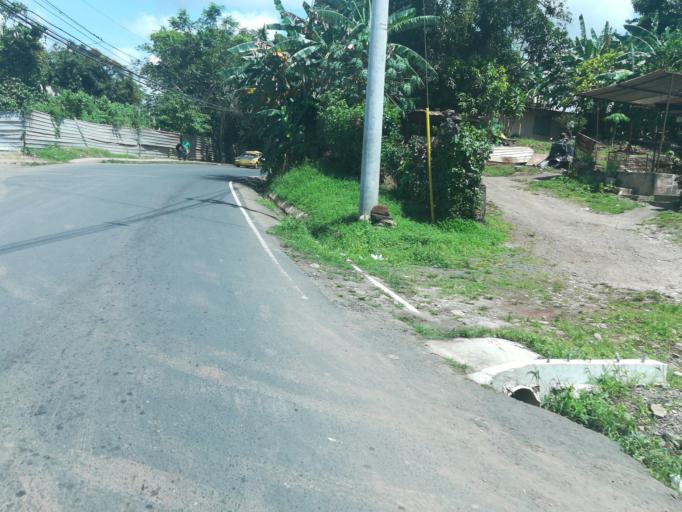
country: PA
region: Panama
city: Tocumen
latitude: 9.0857
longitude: -79.4070
